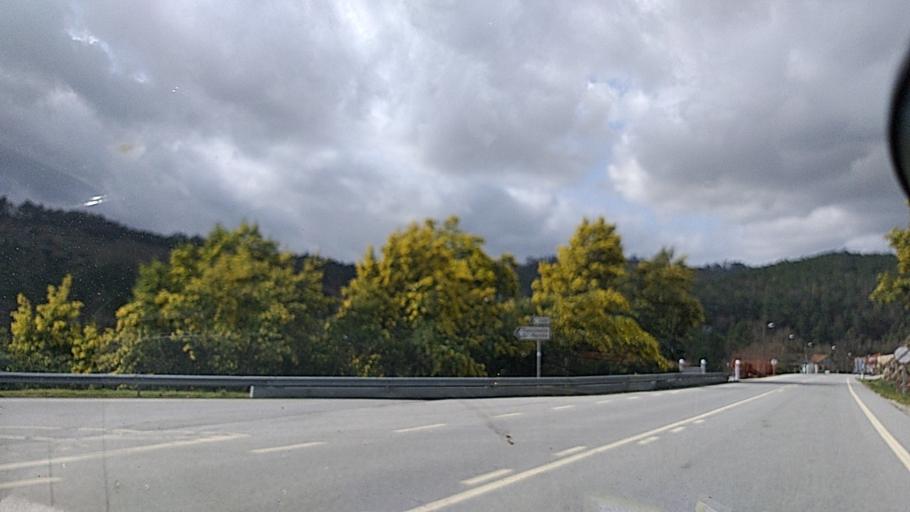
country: PT
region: Viseu
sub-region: Mangualde
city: Mangualde
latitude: 40.6466
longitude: -7.7306
